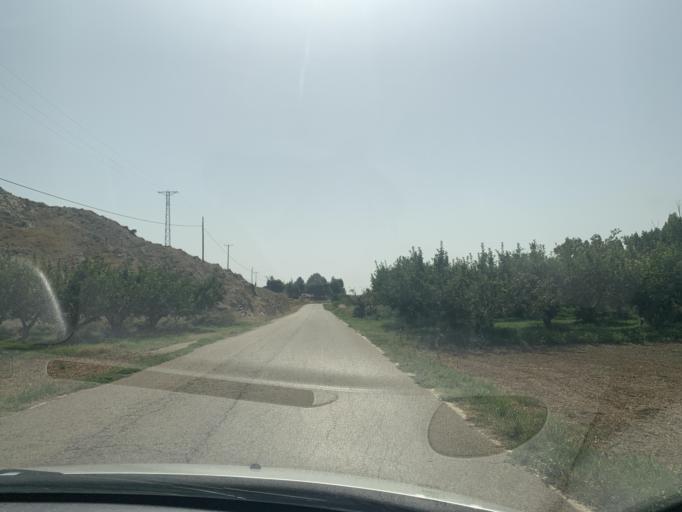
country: ES
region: Aragon
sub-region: Provincia de Zaragoza
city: Almonacid de la Cuba
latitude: 41.2744
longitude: -0.7873
